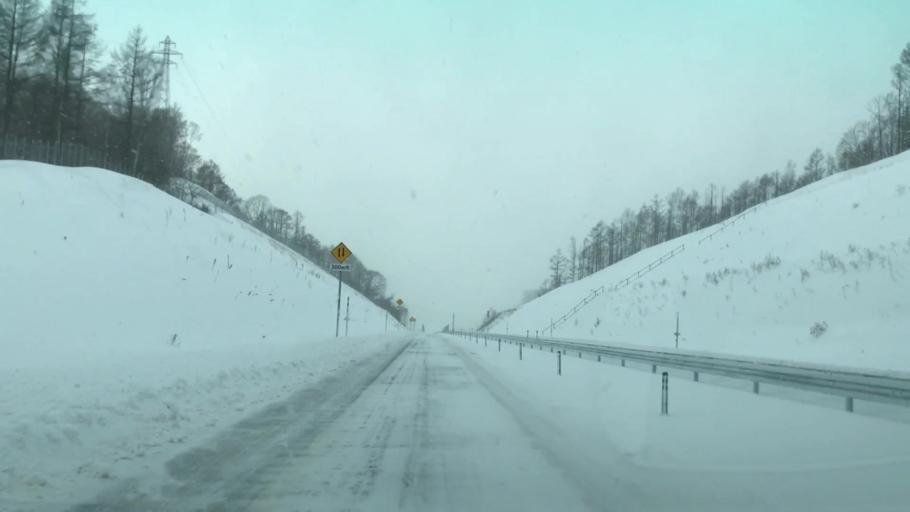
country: JP
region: Hokkaido
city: Otaru
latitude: 43.1971
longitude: 140.9129
